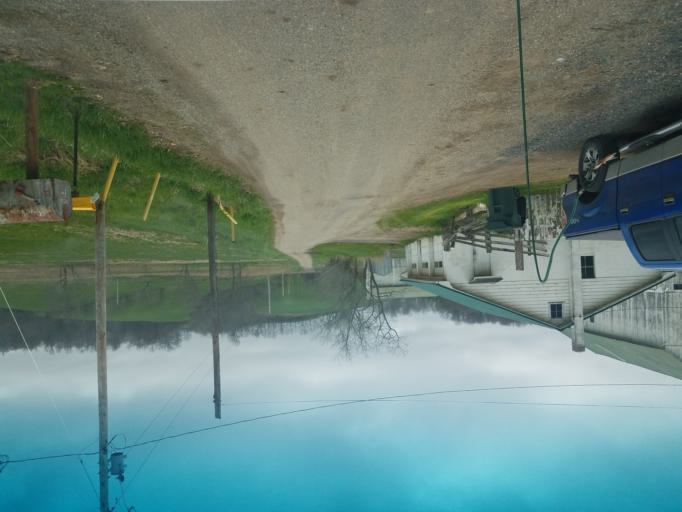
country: US
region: Ohio
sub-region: Stark County
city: Beach City
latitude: 40.6117
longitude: -81.6619
